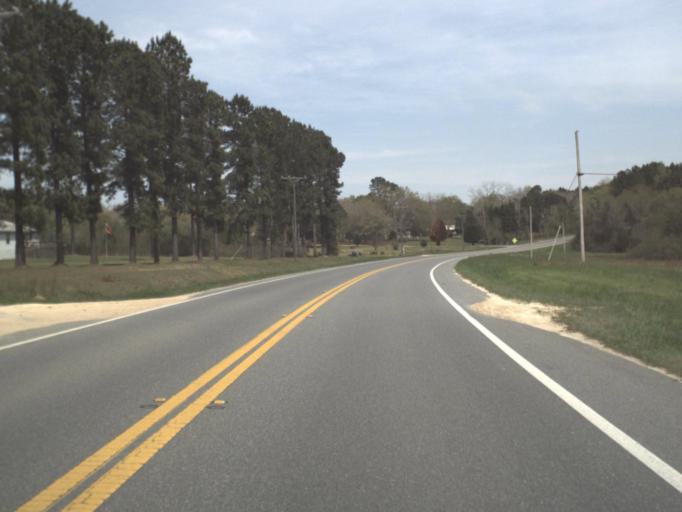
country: US
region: Florida
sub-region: Jackson County
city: Graceville
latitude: 30.9708
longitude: -85.6402
